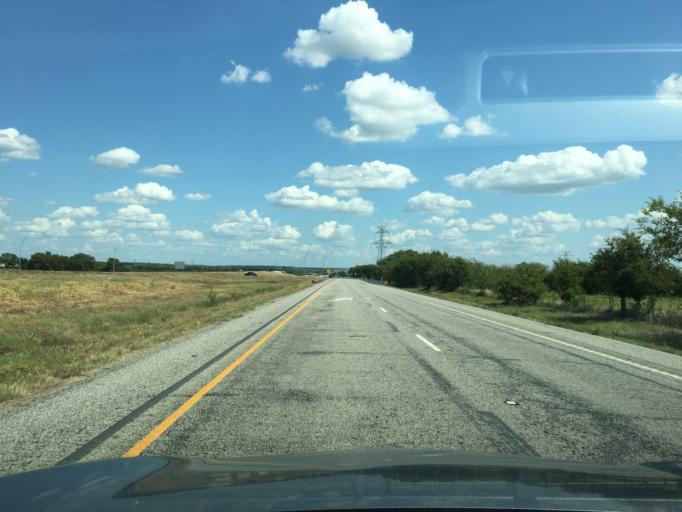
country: US
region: Texas
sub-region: Tarrant County
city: Mansfield
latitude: 32.5199
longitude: -97.0797
